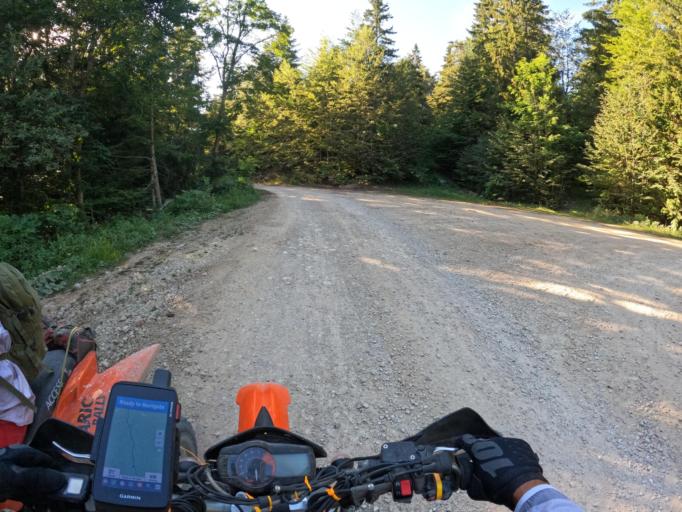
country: BA
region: Federation of Bosnia and Herzegovina
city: Glamoc
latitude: 44.2370
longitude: 16.7741
